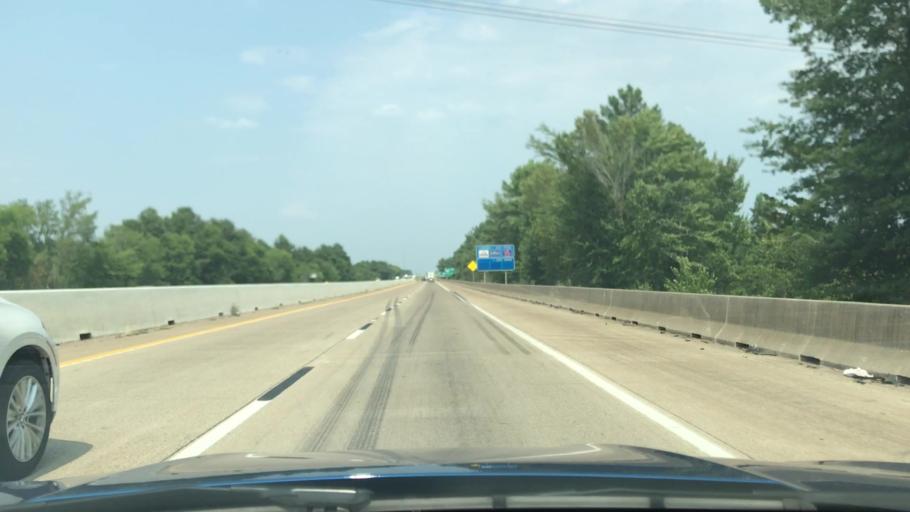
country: US
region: Texas
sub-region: Gregg County
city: Longview
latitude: 32.4398
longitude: -94.7377
